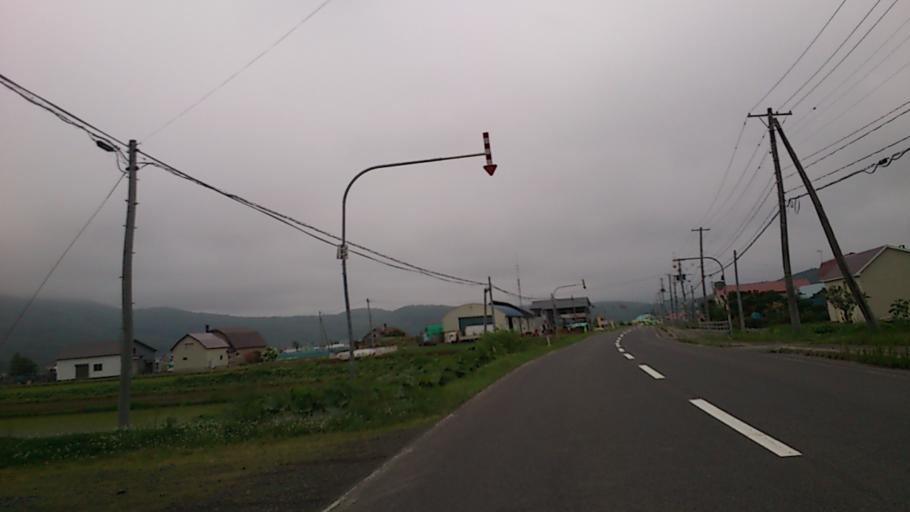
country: JP
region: Hokkaido
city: Niseko Town
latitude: 42.8012
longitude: 140.5033
